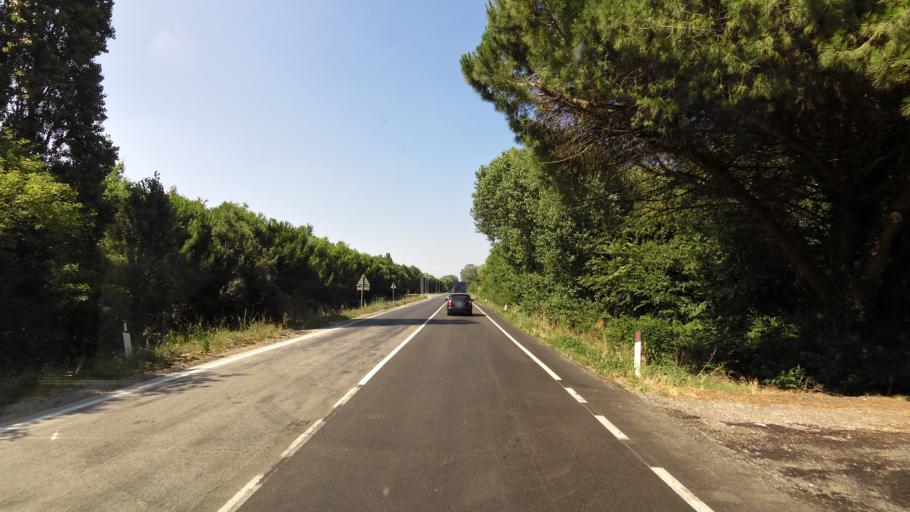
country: IT
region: Emilia-Romagna
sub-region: Provincia di Ravenna
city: Ravenna
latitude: 44.4776
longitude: 12.2104
